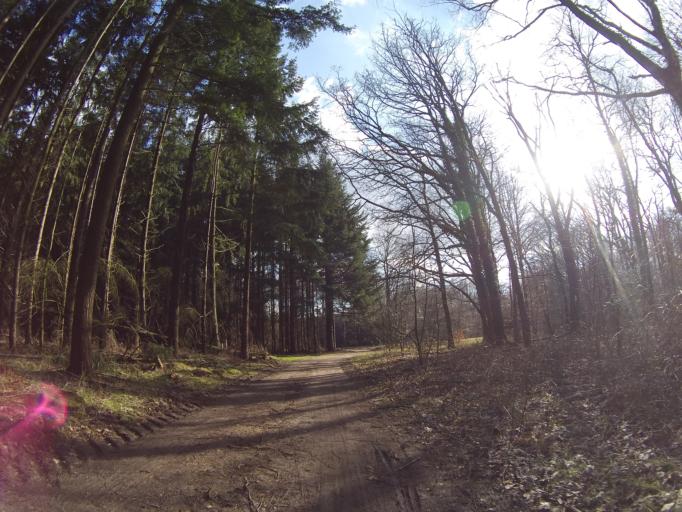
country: NL
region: Utrecht
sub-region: Gemeente Zeist
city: Zeist
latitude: 52.1350
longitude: 5.2574
